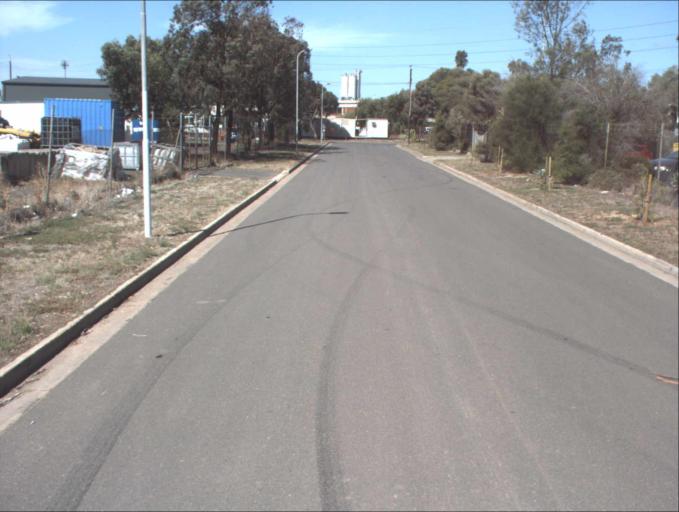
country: AU
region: South Australia
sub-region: Port Adelaide Enfield
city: Enfield
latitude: -34.8344
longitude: 138.5891
